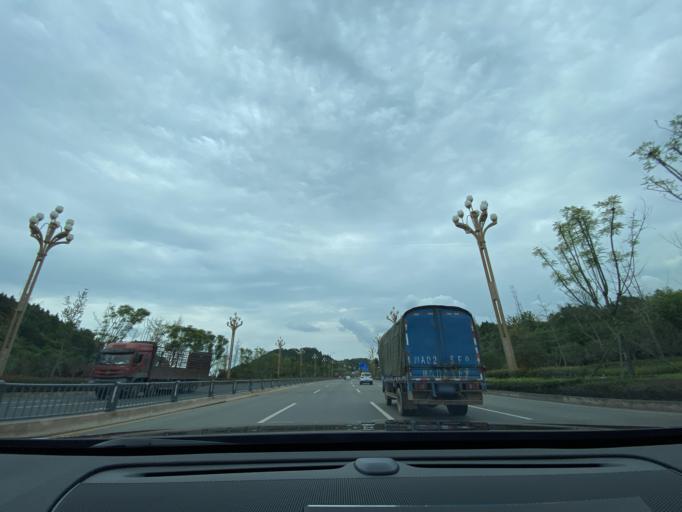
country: CN
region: Sichuan
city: Jiancheng
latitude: 30.4706
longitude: 104.4932
